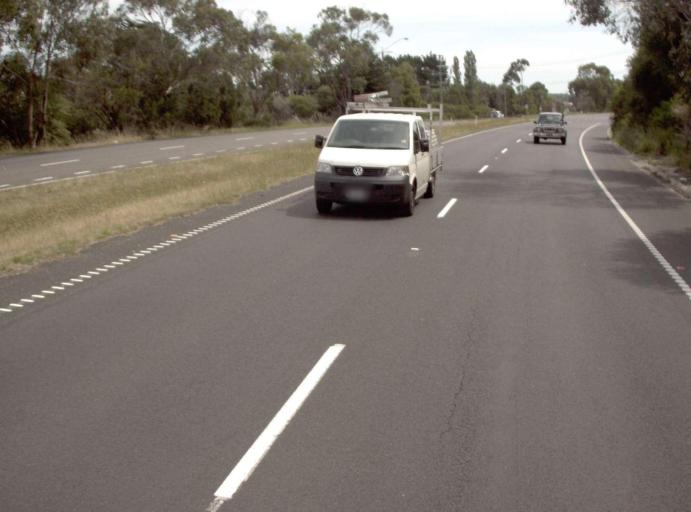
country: AU
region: Victoria
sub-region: Mornington Peninsula
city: Baxter
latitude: -38.1997
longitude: 145.1291
